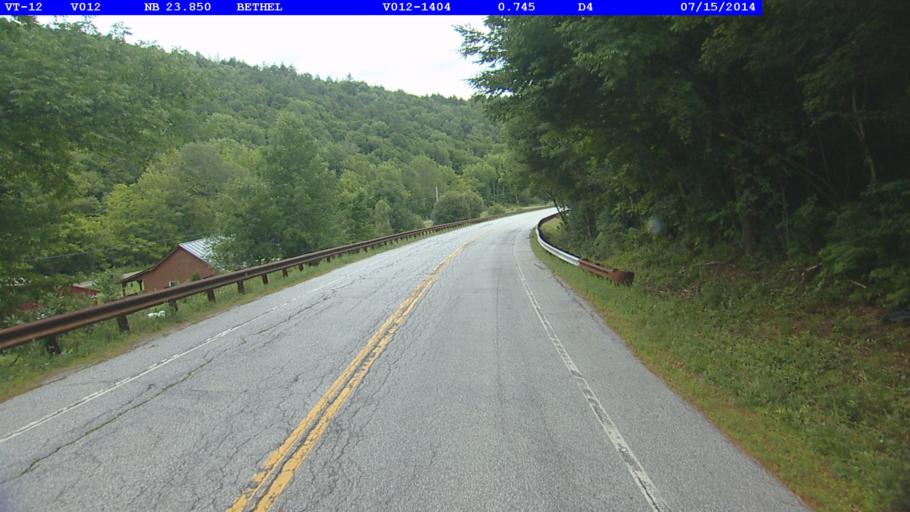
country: US
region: Vermont
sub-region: Orange County
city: Randolph
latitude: 43.8011
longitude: -72.6527
